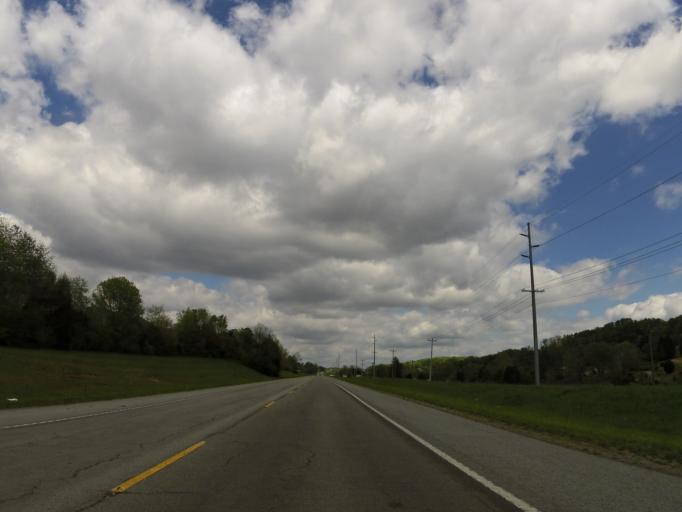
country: US
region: Tennessee
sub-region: Campbell County
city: Fincastle
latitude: 36.4654
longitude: -83.8631
